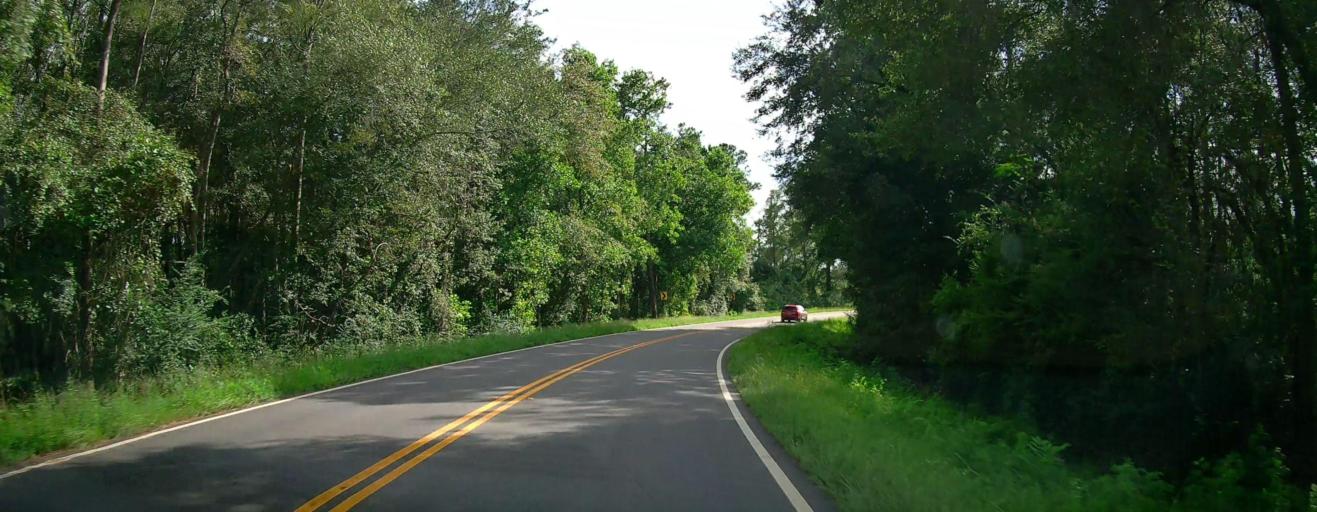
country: US
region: Georgia
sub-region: Coffee County
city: Douglas
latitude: 31.4492
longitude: -82.8679
